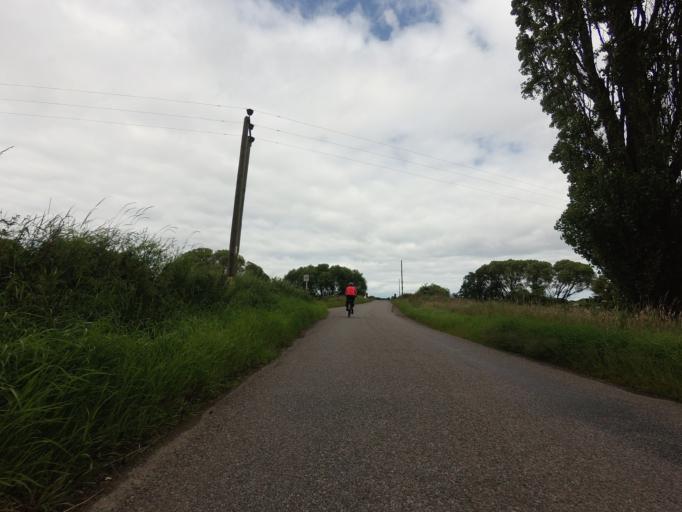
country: GB
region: Scotland
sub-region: Moray
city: Forres
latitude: 57.6221
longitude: -3.6508
